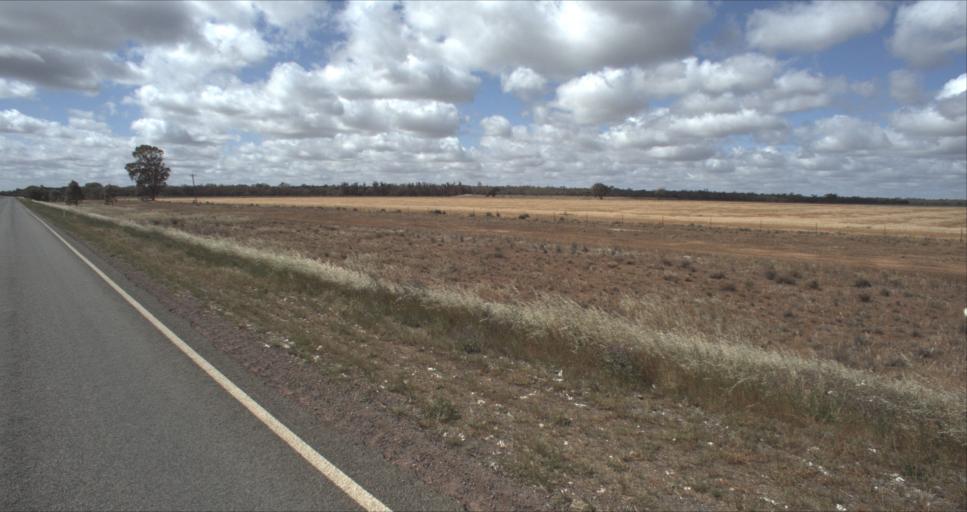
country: AU
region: New South Wales
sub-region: Murrumbidgee Shire
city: Darlington Point
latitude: -34.5906
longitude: 146.1344
